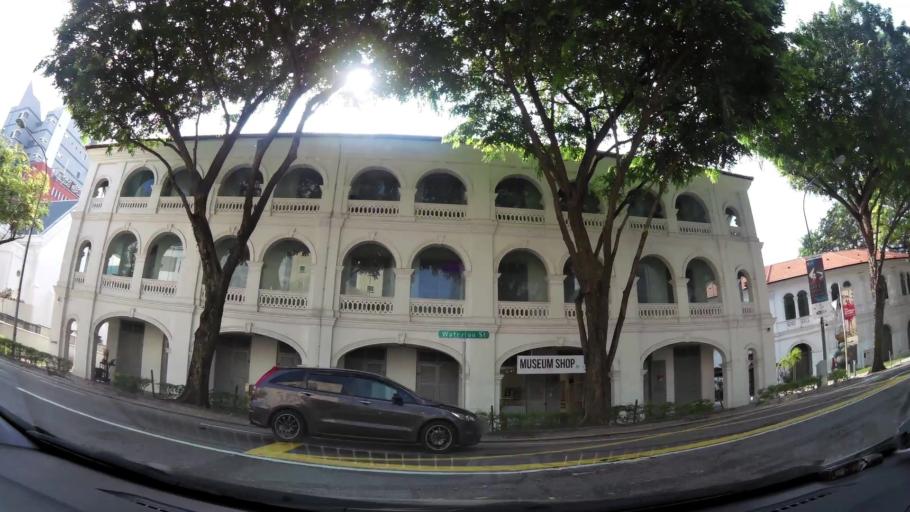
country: SG
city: Singapore
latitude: 1.2978
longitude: 103.8507
